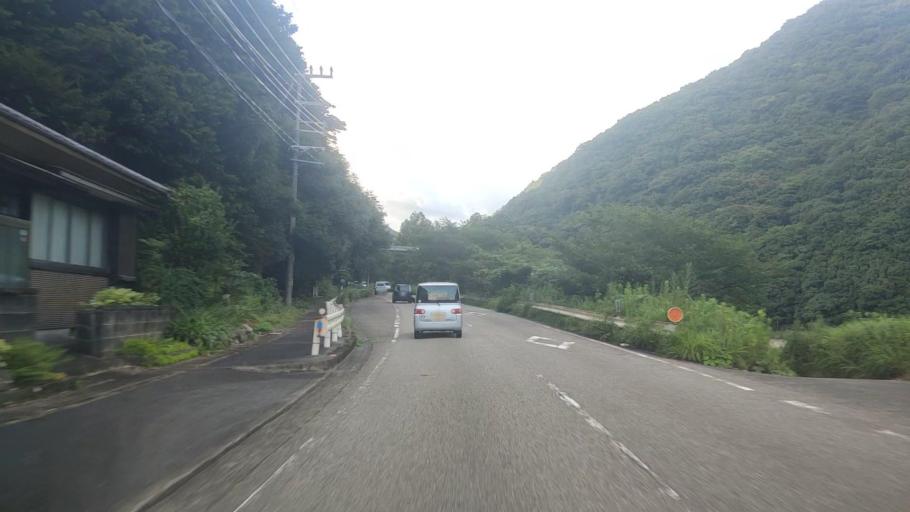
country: JP
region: Wakayama
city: Tanabe
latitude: 33.7631
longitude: 135.5005
